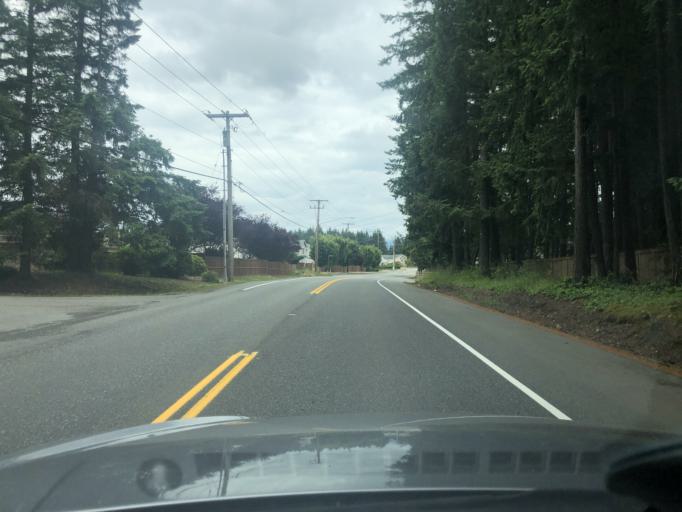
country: US
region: Washington
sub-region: King County
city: Lake Morton-Berrydale
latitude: 47.3418
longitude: -122.0608
